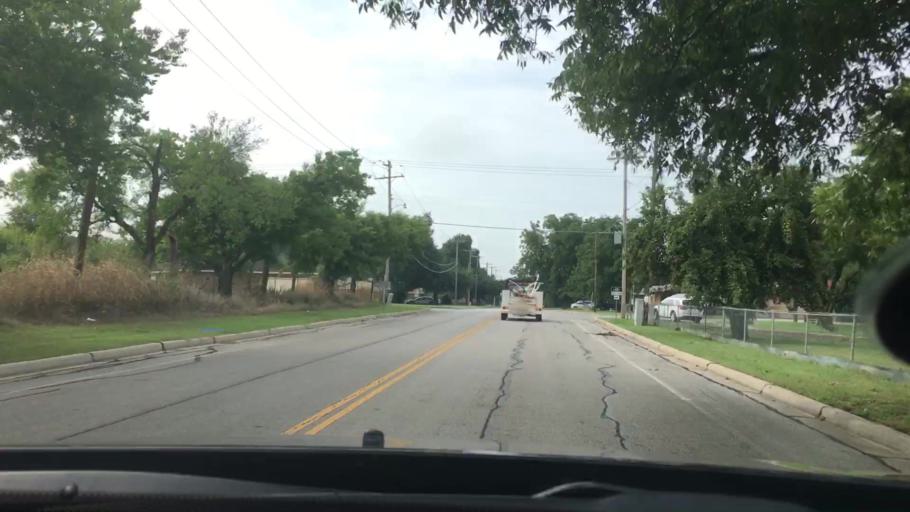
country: US
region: Oklahoma
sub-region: Carter County
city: Ardmore
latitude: 34.1954
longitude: -97.1256
